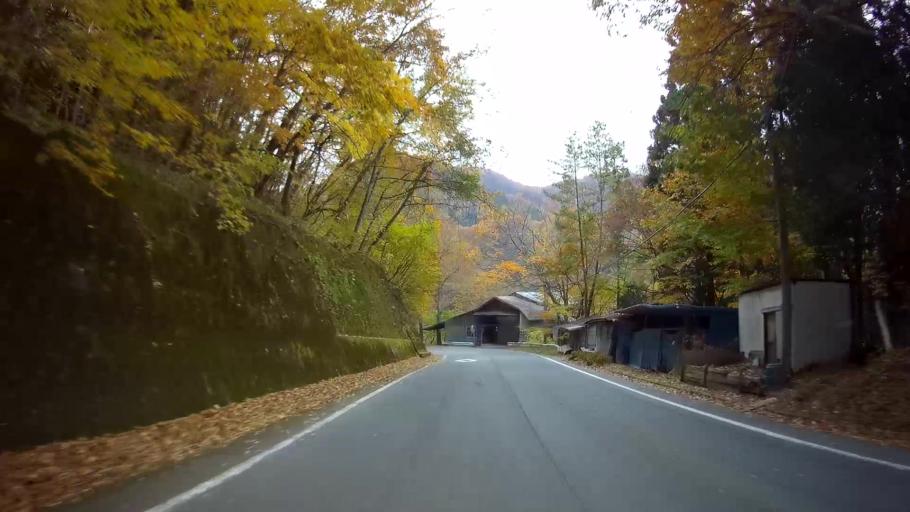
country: JP
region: Gunma
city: Nakanojomachi
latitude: 36.6464
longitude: 138.6503
